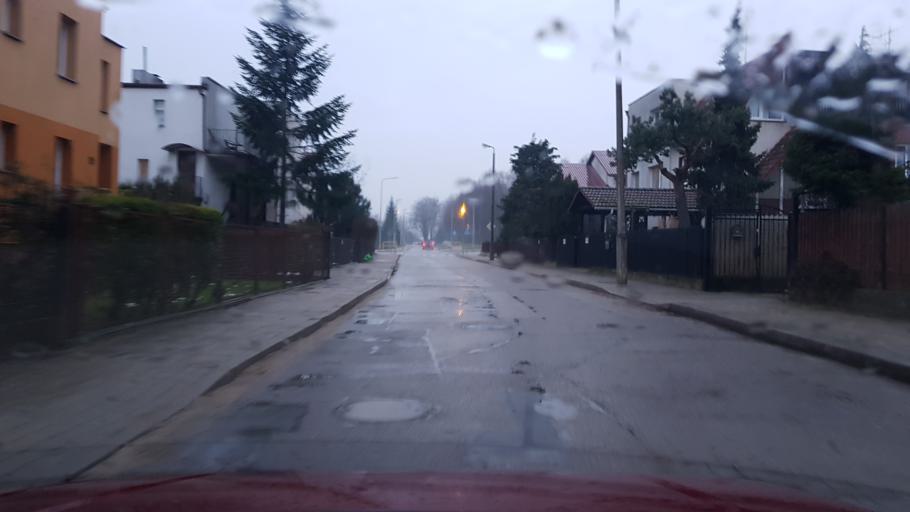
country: PL
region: West Pomeranian Voivodeship
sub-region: Koszalin
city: Koszalin
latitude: 54.1928
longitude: 16.2254
